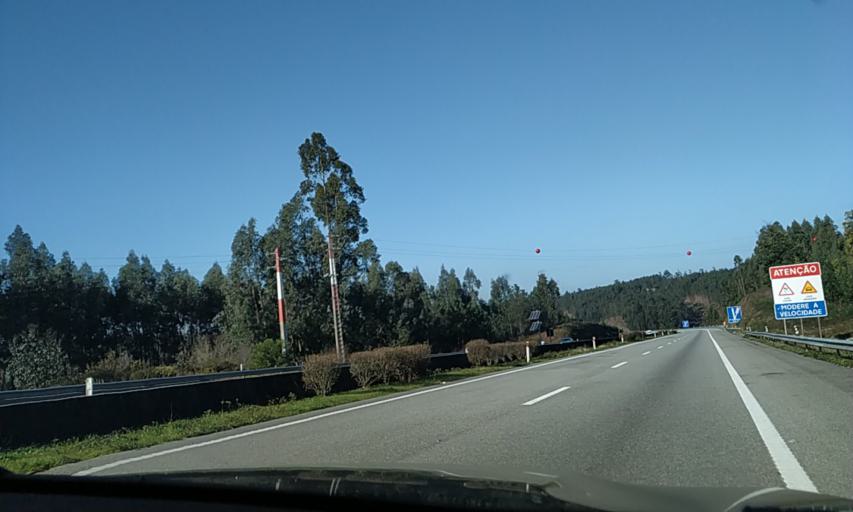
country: PT
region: Aveiro
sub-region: Agueda
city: Valongo
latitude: 40.6629
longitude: -8.3935
